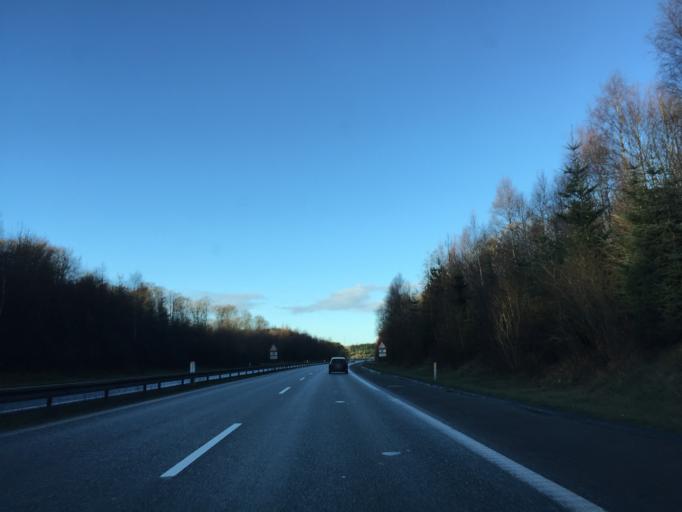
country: DK
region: South Denmark
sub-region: Fredericia Kommune
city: Taulov
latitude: 55.5602
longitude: 9.6250
